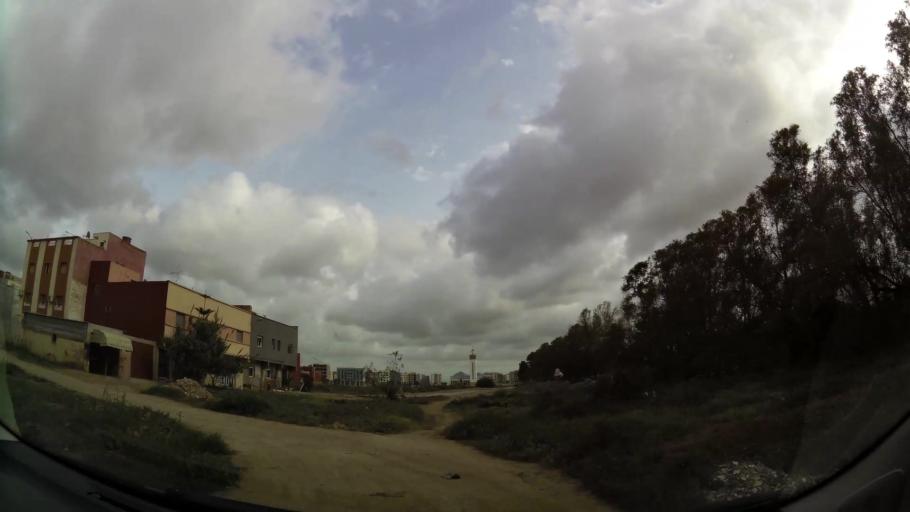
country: MA
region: Oriental
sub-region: Nador
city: Nador
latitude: 35.1572
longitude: -2.9183
